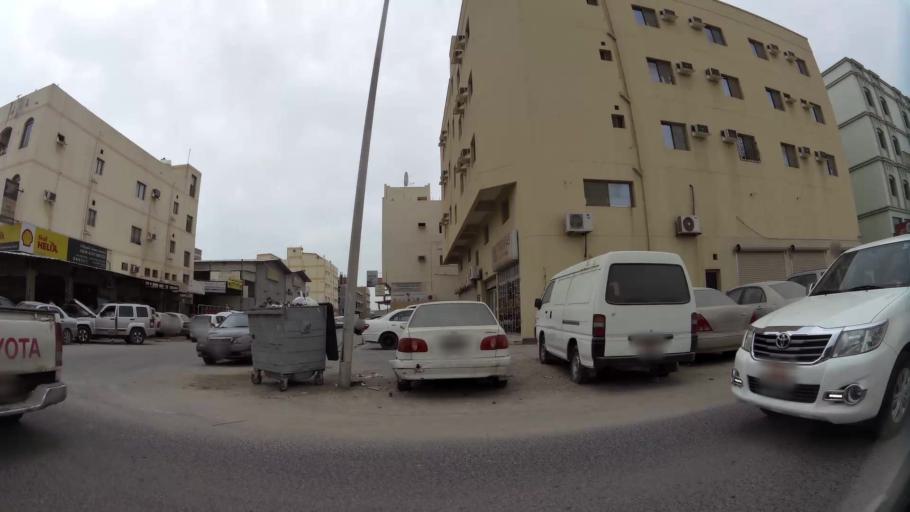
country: BH
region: Northern
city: Madinat `Isa
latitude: 26.1760
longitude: 50.5291
